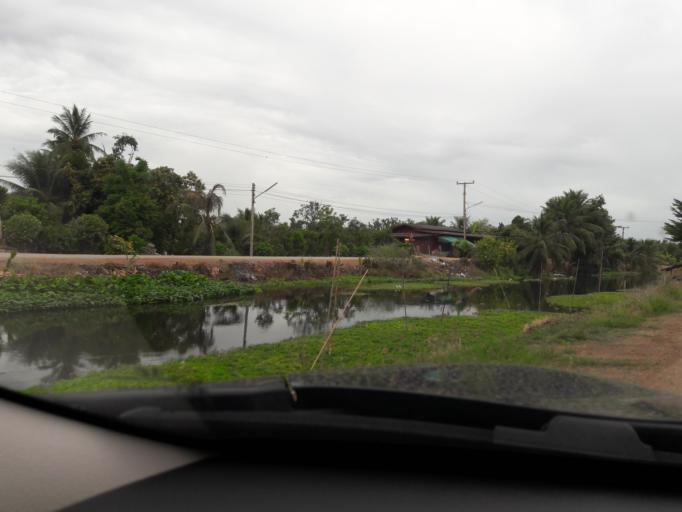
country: TH
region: Ratchaburi
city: Bang Phae
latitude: 13.6181
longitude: 99.9629
